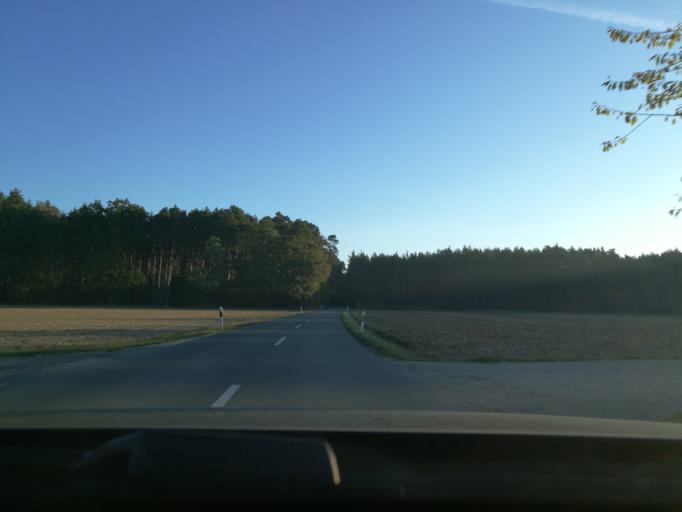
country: DE
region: Bavaria
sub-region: Regierungsbezirk Mittelfranken
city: Tuchenbach
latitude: 49.5381
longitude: 10.8665
